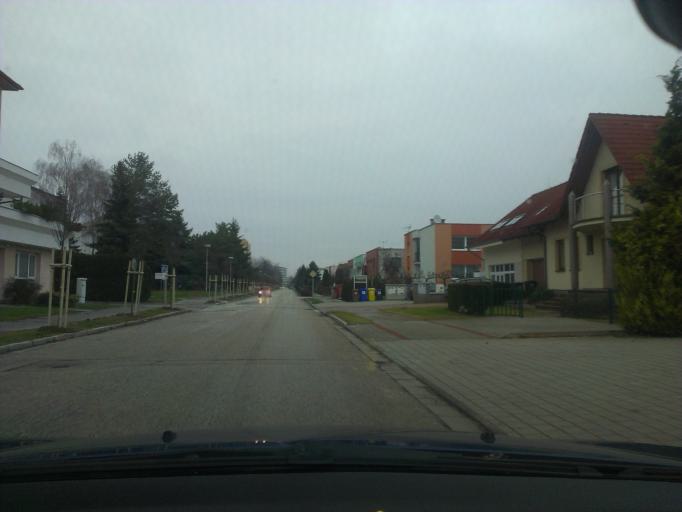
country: SK
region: Trnavsky
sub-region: Okres Trnava
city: Piestany
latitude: 48.5802
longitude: 17.8194
